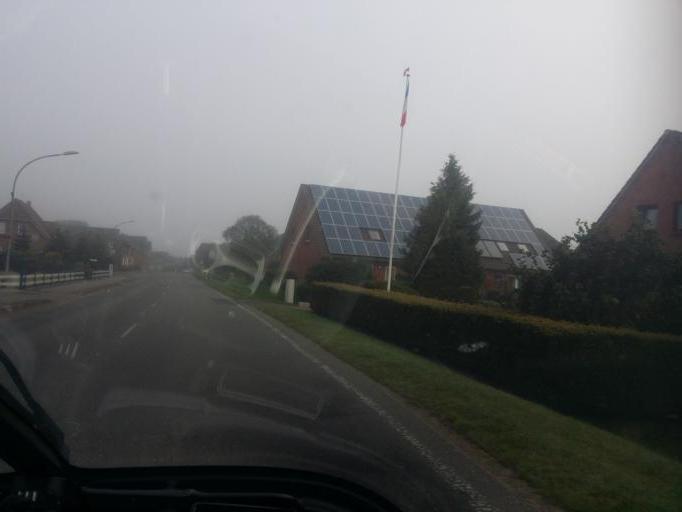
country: DE
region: Schleswig-Holstein
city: Horstedt
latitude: 54.5239
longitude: 9.0688
